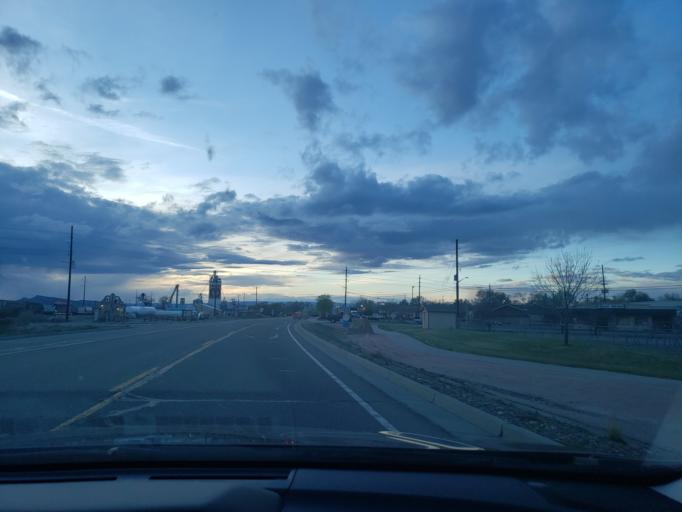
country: US
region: Colorado
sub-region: Mesa County
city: Fruita
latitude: 39.1527
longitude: -108.7278
